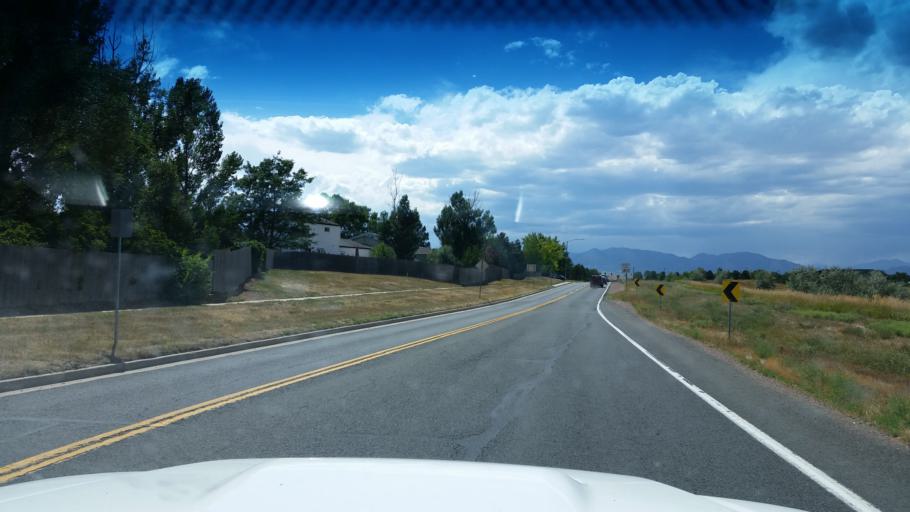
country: US
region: Colorado
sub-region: Broomfield County
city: Broomfield
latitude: 39.8928
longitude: -105.1117
